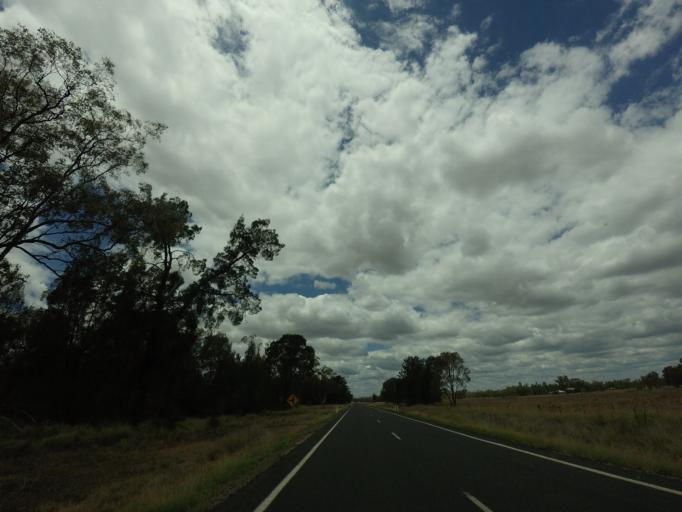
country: AU
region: Queensland
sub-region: Goondiwindi
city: Goondiwindi
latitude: -28.1596
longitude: 150.6396
